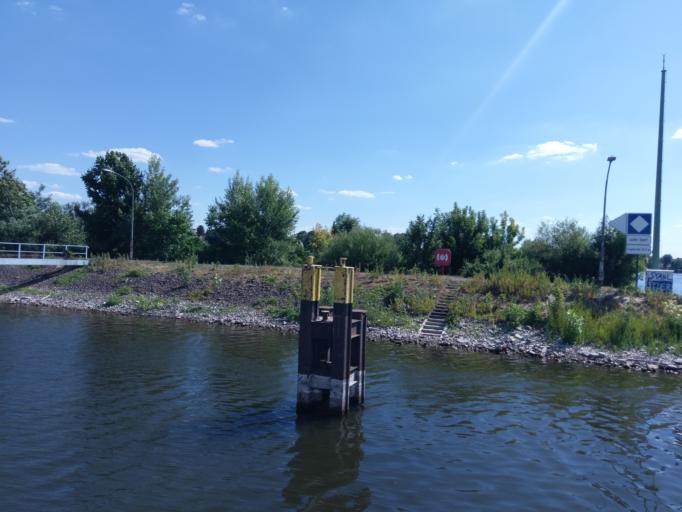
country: DE
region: Brandenburg
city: Brandenburg an der Havel
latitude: 52.4230
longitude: 12.5669
